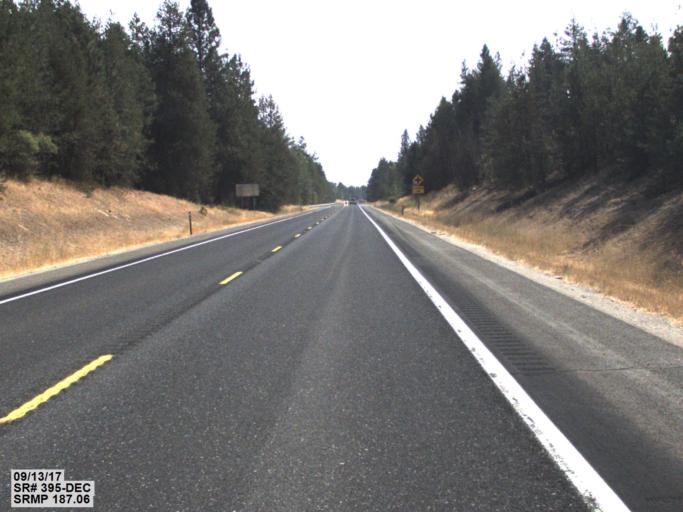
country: US
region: Washington
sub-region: Spokane County
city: Deer Park
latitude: 48.0158
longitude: -117.5870
